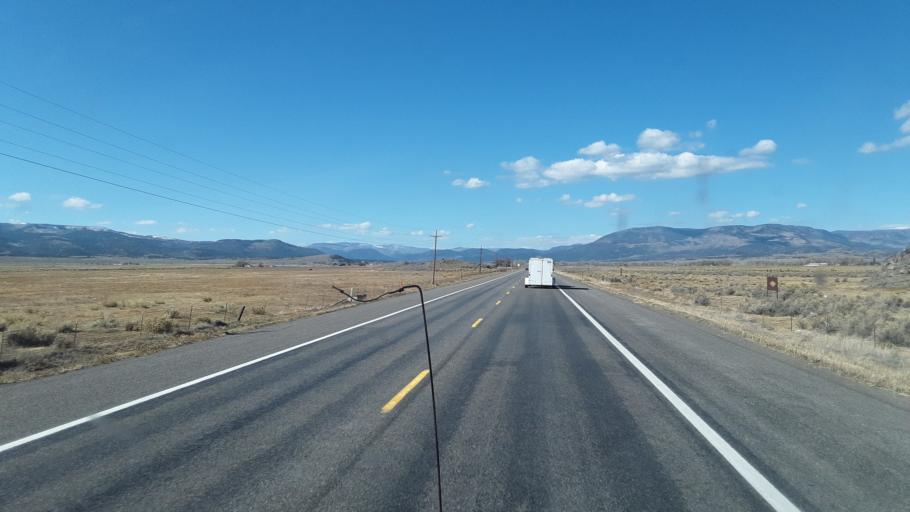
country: US
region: Colorado
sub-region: Rio Grande County
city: Del Norte
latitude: 37.6745
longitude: -106.4195
